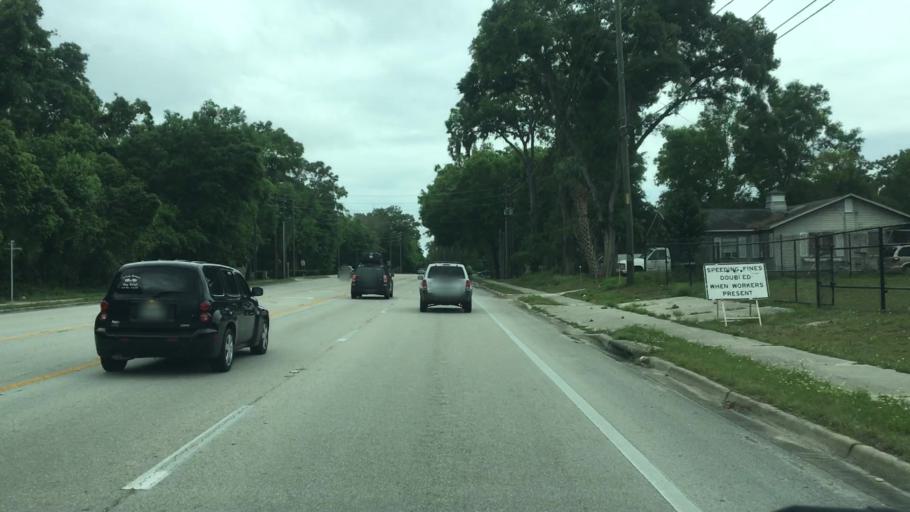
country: US
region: Florida
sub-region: Volusia County
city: De Land Southwest
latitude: 28.9990
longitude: -81.3079
